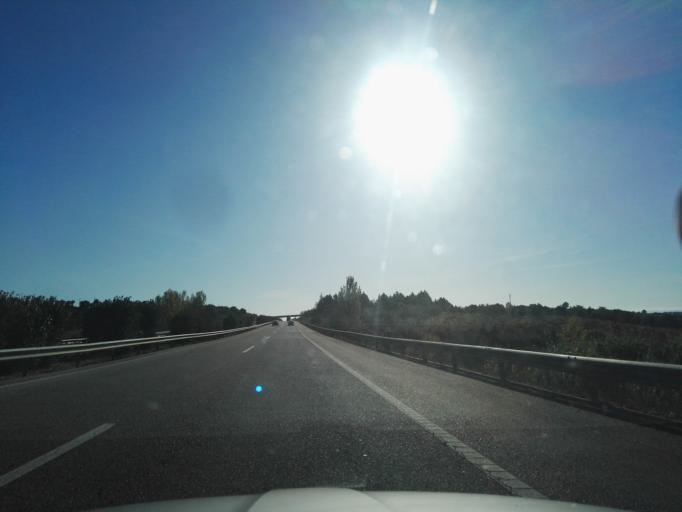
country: PT
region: Santarem
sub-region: Torres Novas
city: Torres Novas
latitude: 39.4699
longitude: -8.5708
